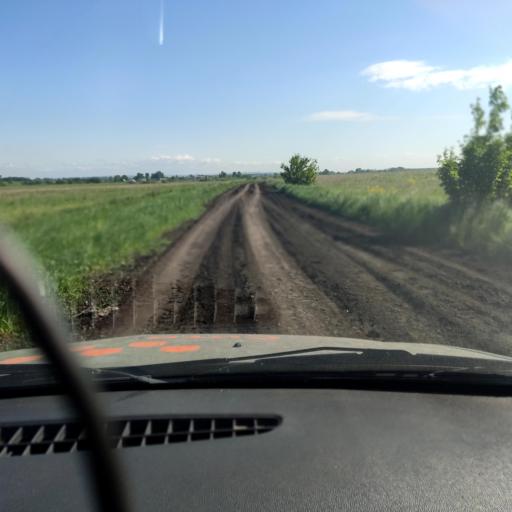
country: RU
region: Bashkortostan
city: Avdon
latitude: 54.5670
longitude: 55.8322
